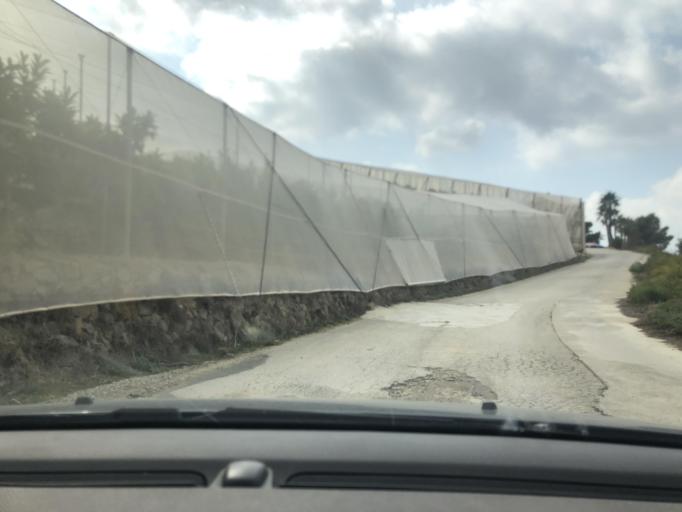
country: ES
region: Valencia
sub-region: Provincia de Alicante
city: Callosa d'En Sarria
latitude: 38.6534
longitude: -0.0896
